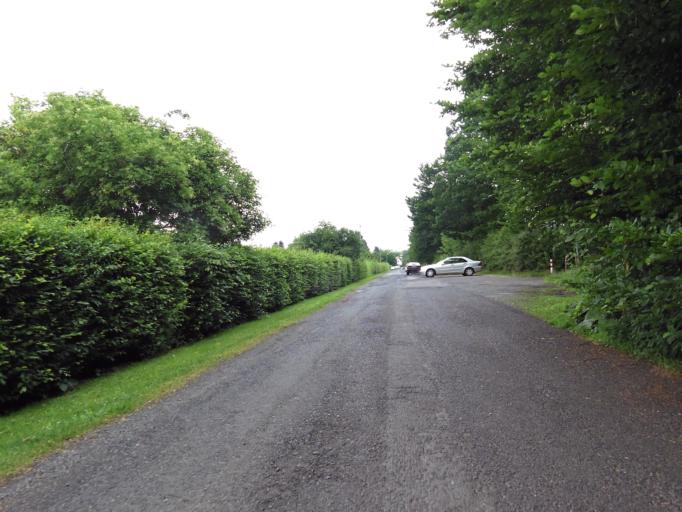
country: DE
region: Lower Saxony
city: Goettingen
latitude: 51.5162
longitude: 9.9476
